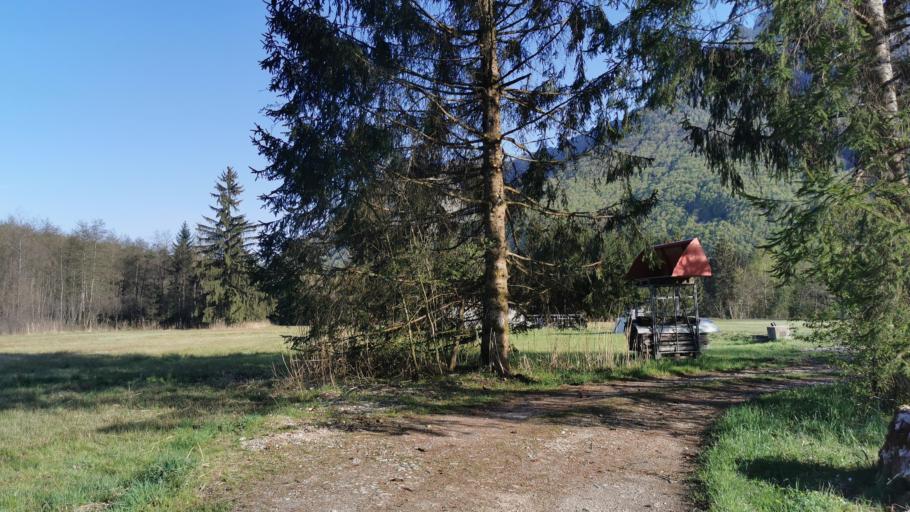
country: AT
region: Salzburg
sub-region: Politischer Bezirk Salzburg-Umgebung
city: Grodig
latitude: 47.7519
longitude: 13.0006
